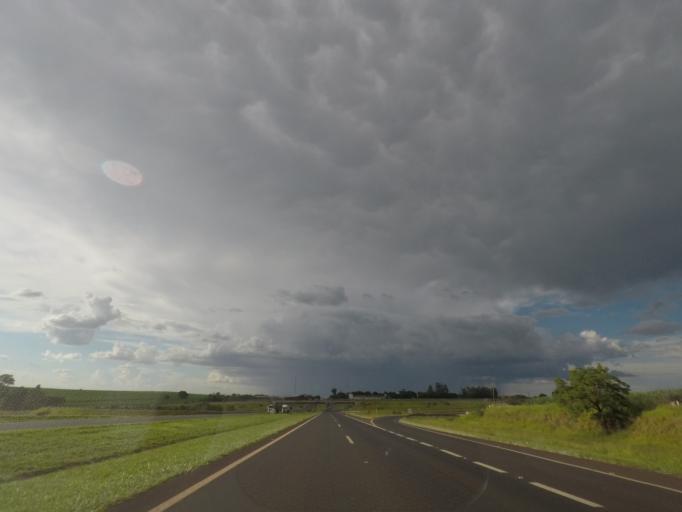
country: BR
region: Sao Paulo
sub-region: Jardinopolis
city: Jardinopolis
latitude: -21.0527
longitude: -47.8240
